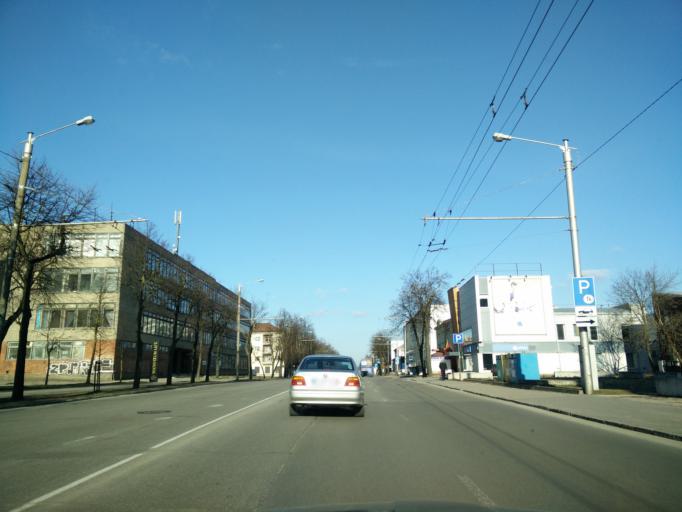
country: LT
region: Kauno apskritis
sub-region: Kaunas
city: Eiguliai
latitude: 54.9091
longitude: 23.9297
